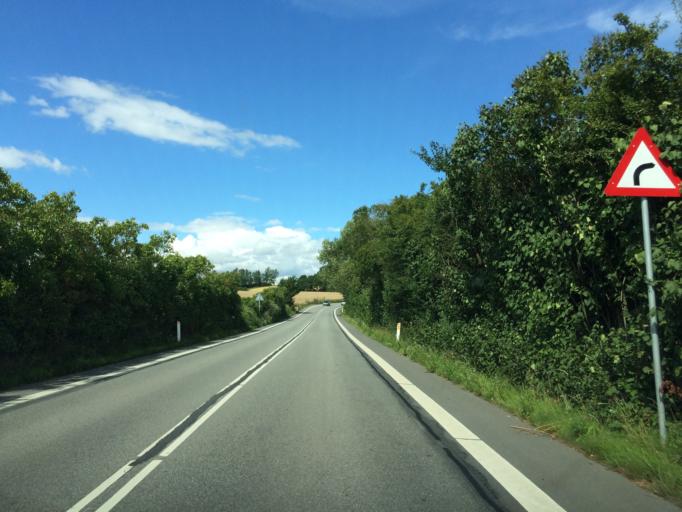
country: DK
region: South Denmark
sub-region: Faaborg-Midtfyn Kommune
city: Faaborg
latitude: 55.1223
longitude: 10.2126
